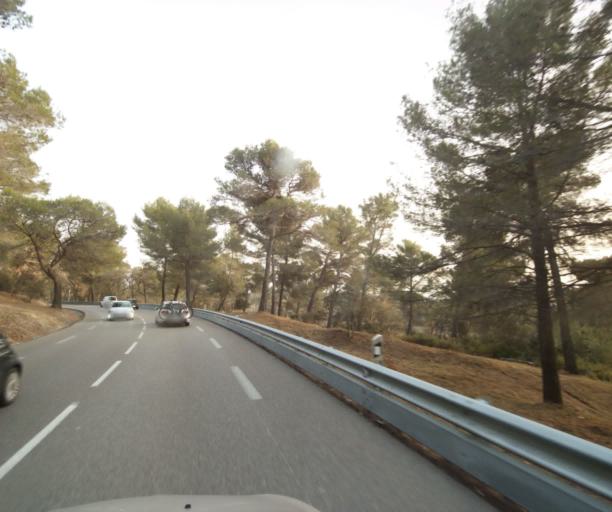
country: FR
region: Provence-Alpes-Cote d'Azur
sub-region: Departement des Bouches-du-Rhone
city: Rognes
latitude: 43.6199
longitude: 5.3541
